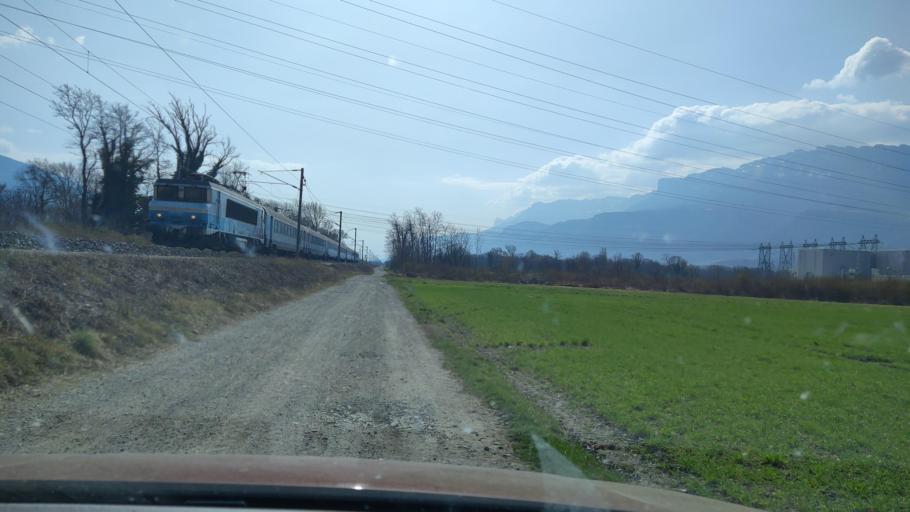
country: FR
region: Rhone-Alpes
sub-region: Departement de la Savoie
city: Montmelian
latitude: 45.4709
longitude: 6.0352
